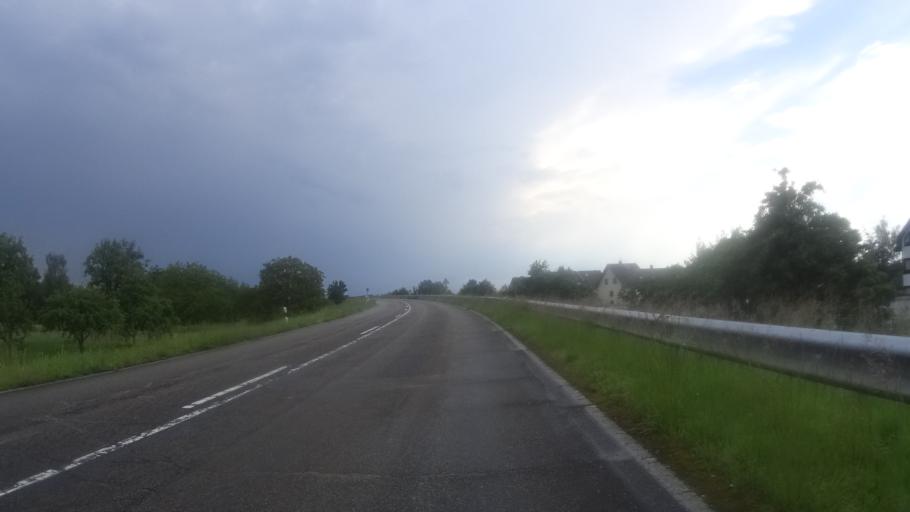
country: DE
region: Baden-Wuerttemberg
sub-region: Karlsruhe Region
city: Bietigheim
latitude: 48.9013
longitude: 8.2494
